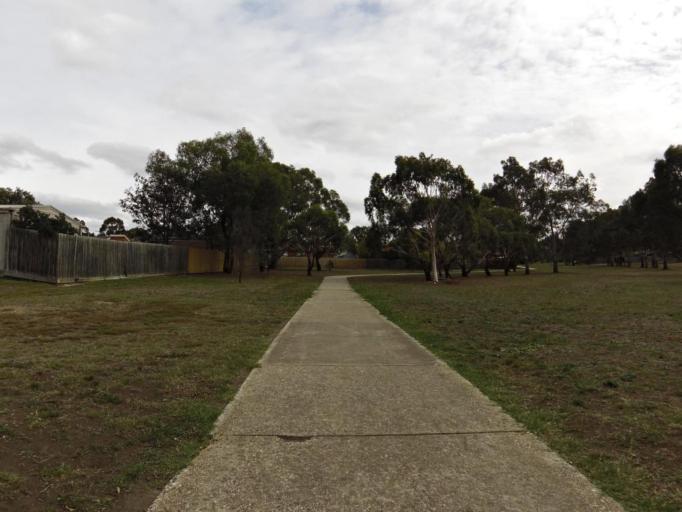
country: AU
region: Victoria
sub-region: Hume
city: Sunbury
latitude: -37.5734
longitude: 144.7027
